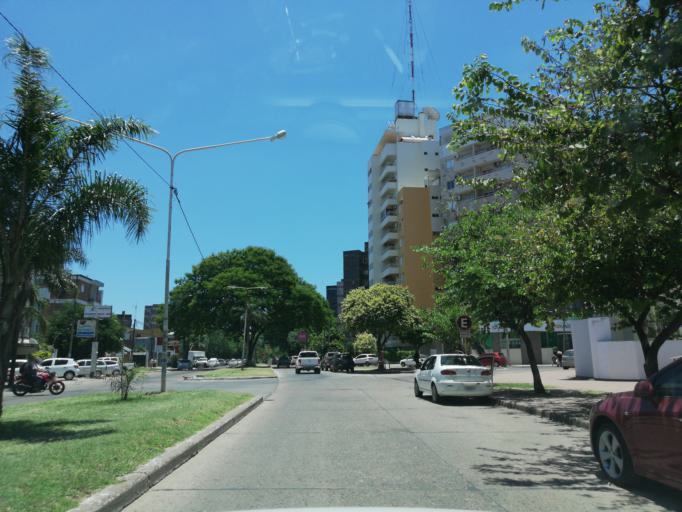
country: AR
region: Corrientes
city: Corrientes
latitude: -27.4647
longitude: -58.8245
